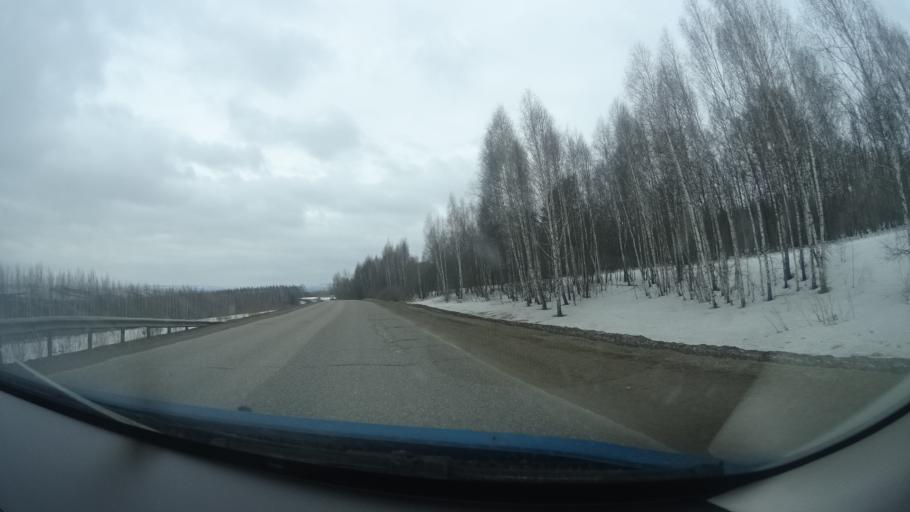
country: RU
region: Bashkortostan
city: Birsk
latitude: 55.2865
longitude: 55.6519
